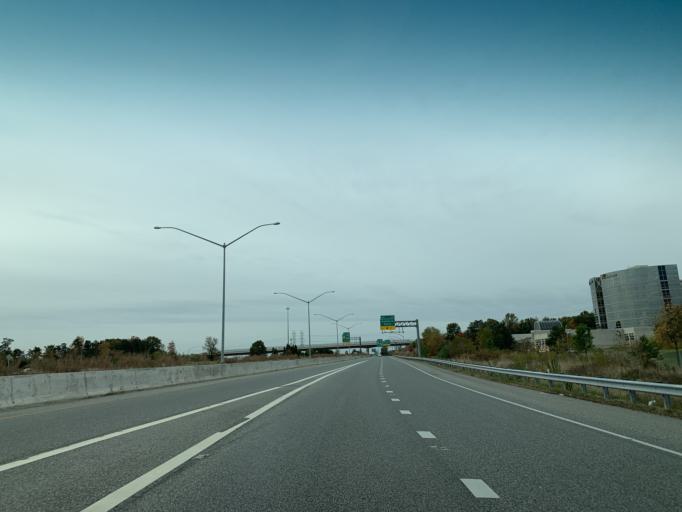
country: US
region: Maryland
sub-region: Prince George's County
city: West Laurel
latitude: 39.0887
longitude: -76.8950
